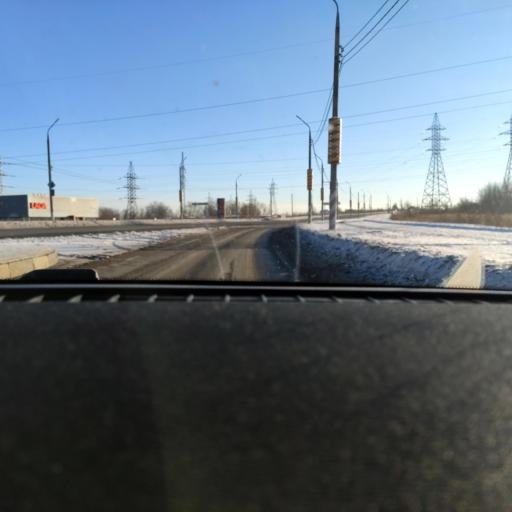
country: RU
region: Samara
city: Novokuybyshevsk
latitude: 53.0859
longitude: 49.9978
